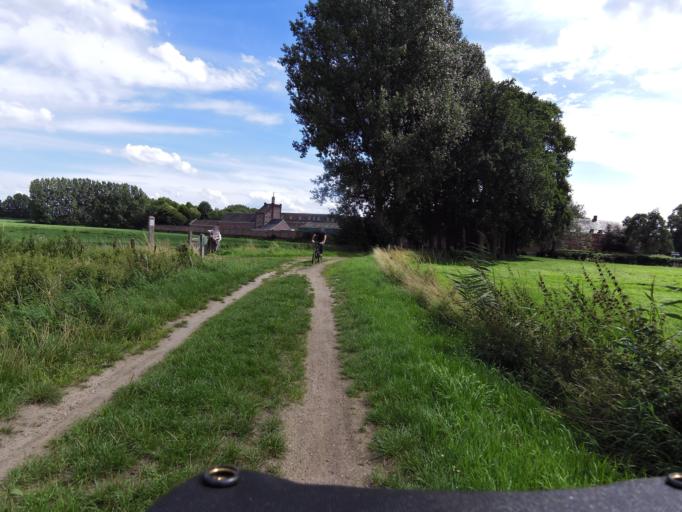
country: BE
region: Flanders
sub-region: Provincie Antwerpen
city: Hoogstraten
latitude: 51.4046
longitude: 4.7787
